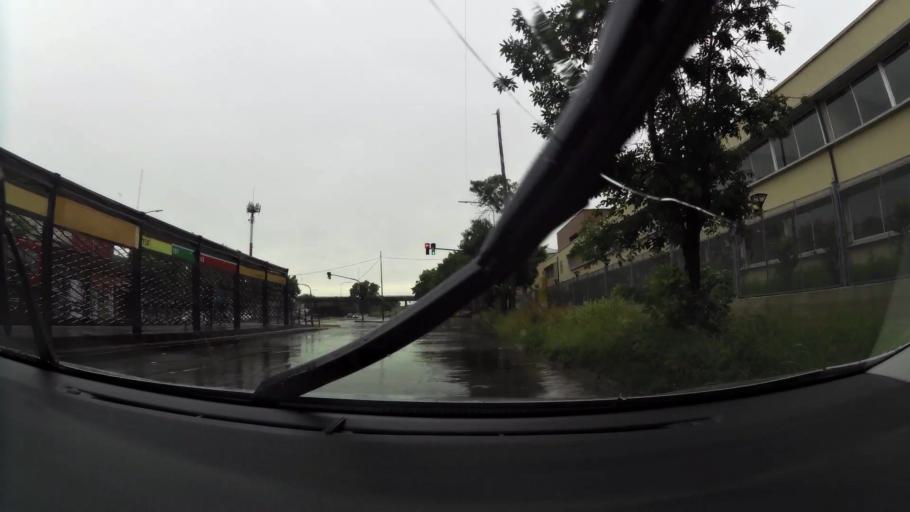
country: AR
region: Buenos Aires F.D.
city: Villa Lugano
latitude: -34.6639
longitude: -58.4485
